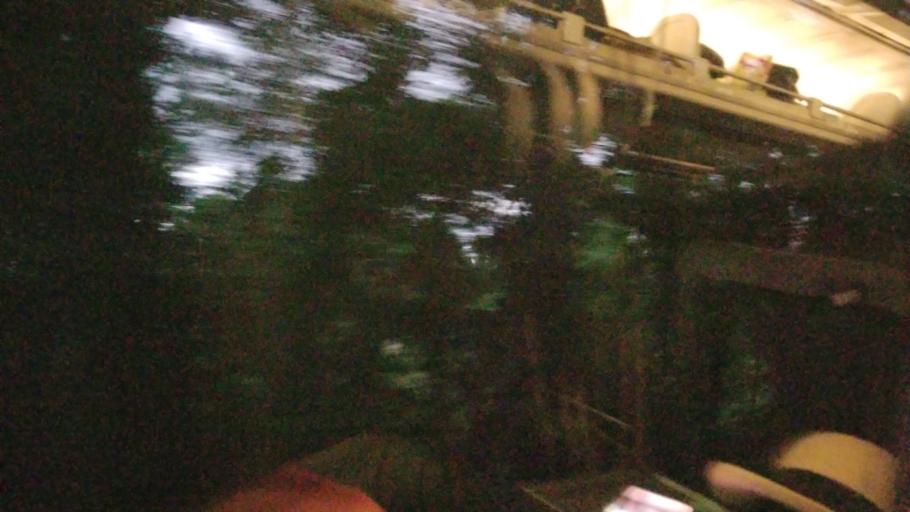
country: US
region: Virginia
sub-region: Orange County
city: Gordonsville
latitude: 38.1764
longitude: -78.2690
